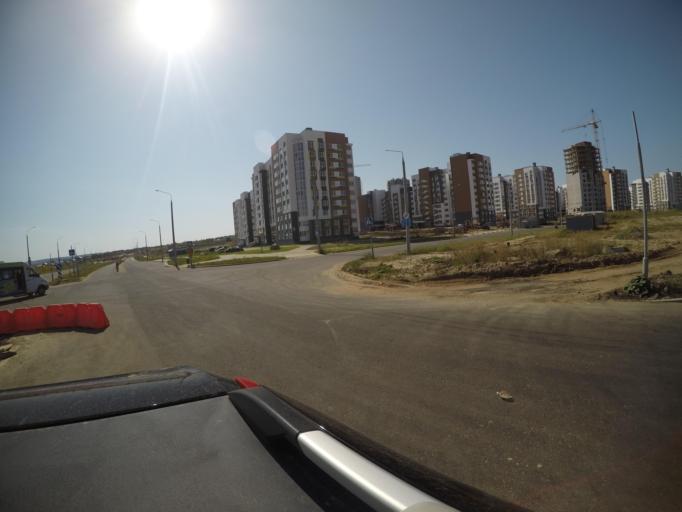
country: BY
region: Grodnenskaya
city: Hrodna
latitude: 53.7236
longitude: 23.8842
